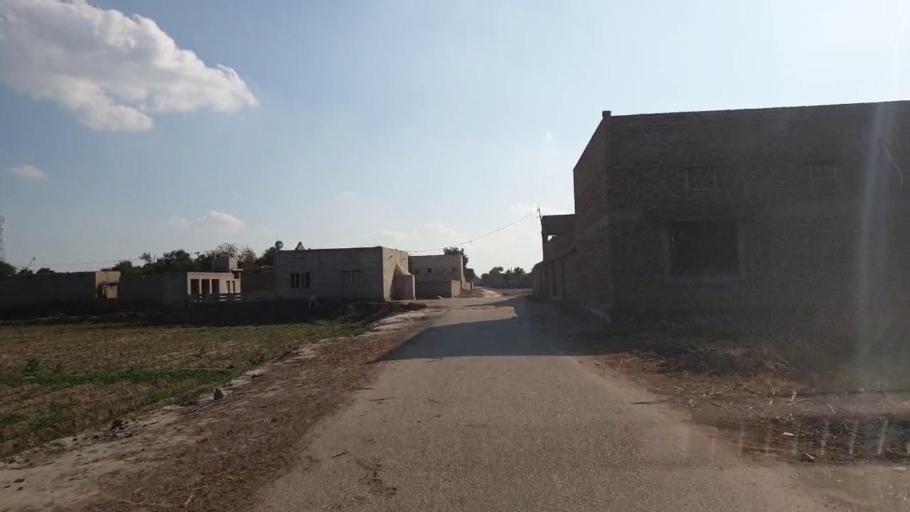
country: PK
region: Sindh
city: Shahpur Chakar
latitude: 26.1058
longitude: 68.5645
